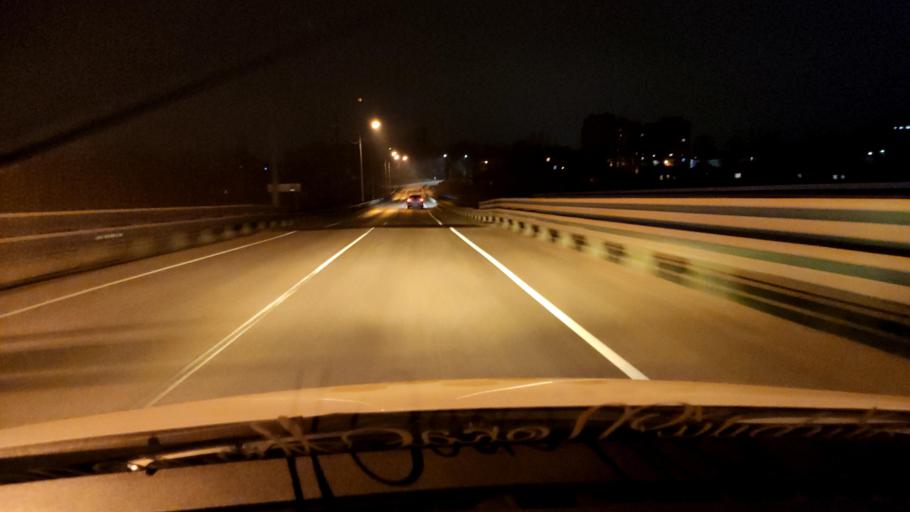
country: RU
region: Voronezj
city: Semiluki
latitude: 51.6752
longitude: 39.0322
